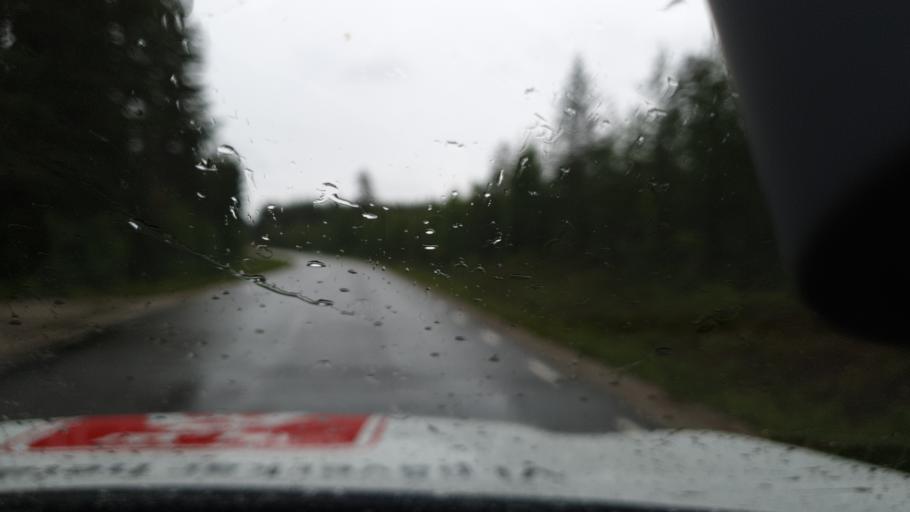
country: SE
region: Vaesterbotten
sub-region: Vindelns Kommun
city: Vindeln
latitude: 64.4111
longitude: 19.6642
